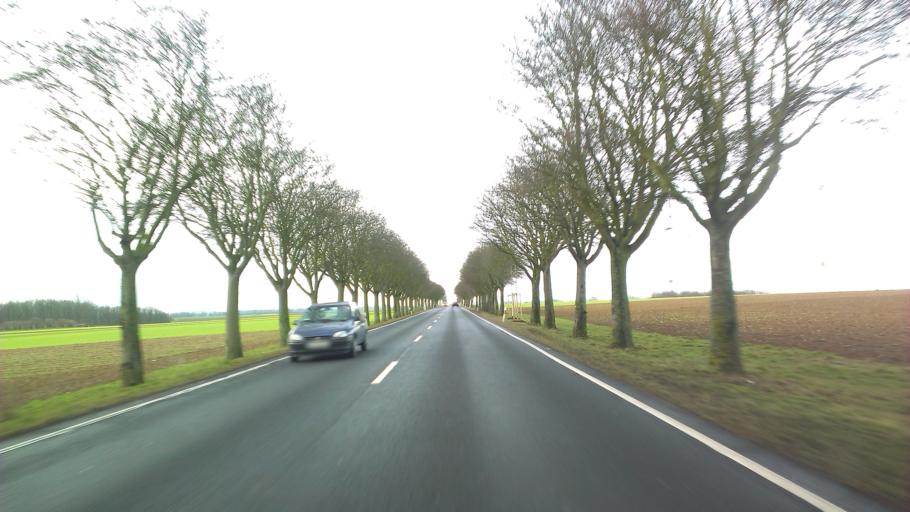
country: DE
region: Rheinland-Pfalz
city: Lonsheim
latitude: 49.7504
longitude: 8.0695
